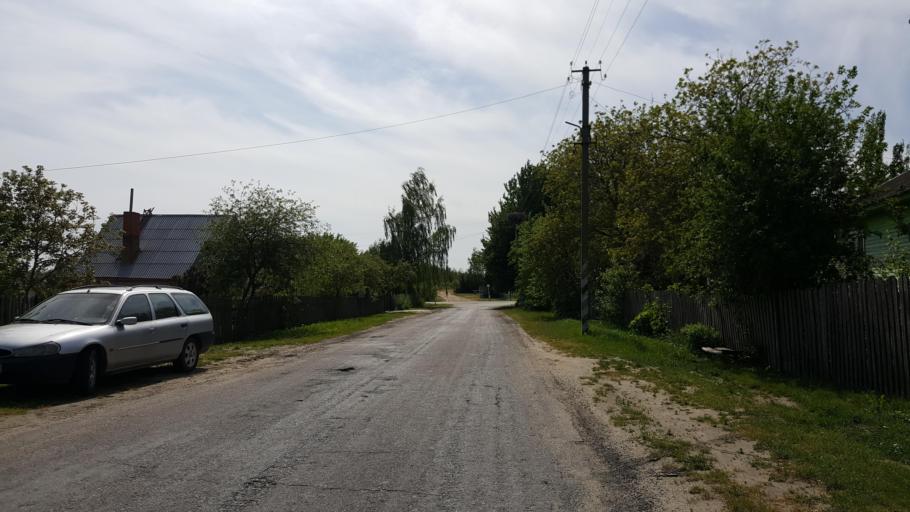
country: BY
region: Brest
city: Charnawchytsy
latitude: 52.2513
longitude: 23.6127
